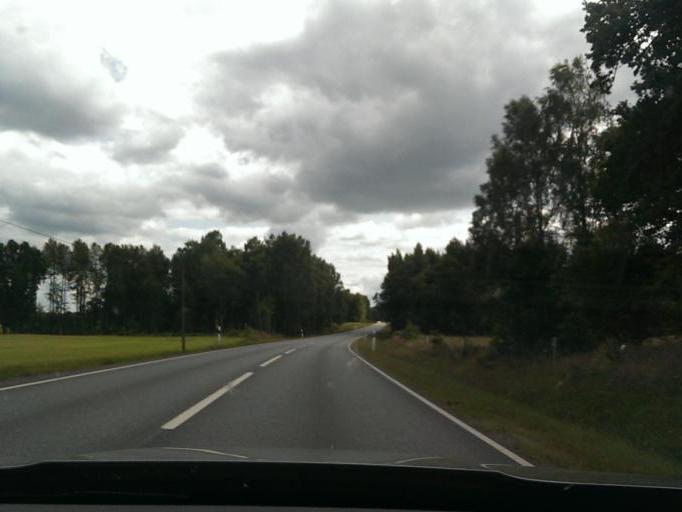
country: SE
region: Joenkoeping
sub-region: Varnamo Kommun
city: Varnamo
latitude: 57.2367
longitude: 14.0053
